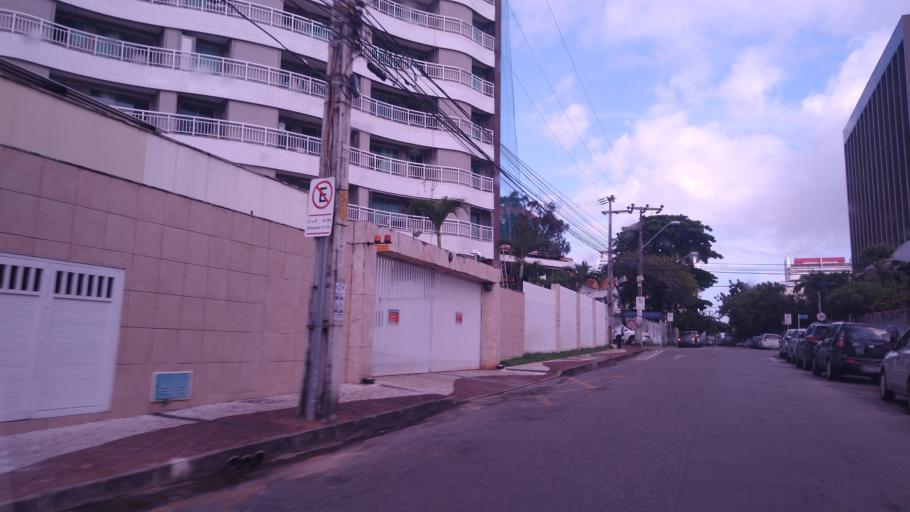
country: BR
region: Ceara
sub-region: Fortaleza
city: Fortaleza
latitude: -3.7387
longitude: -38.4943
